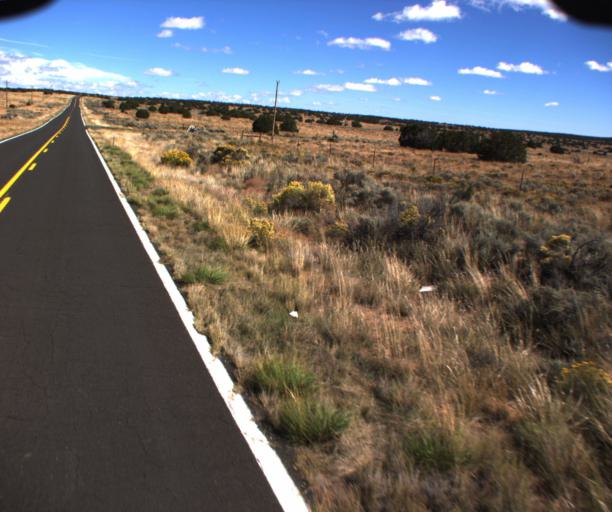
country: US
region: New Mexico
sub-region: McKinley County
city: Zuni Pueblo
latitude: 34.9771
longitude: -109.1324
